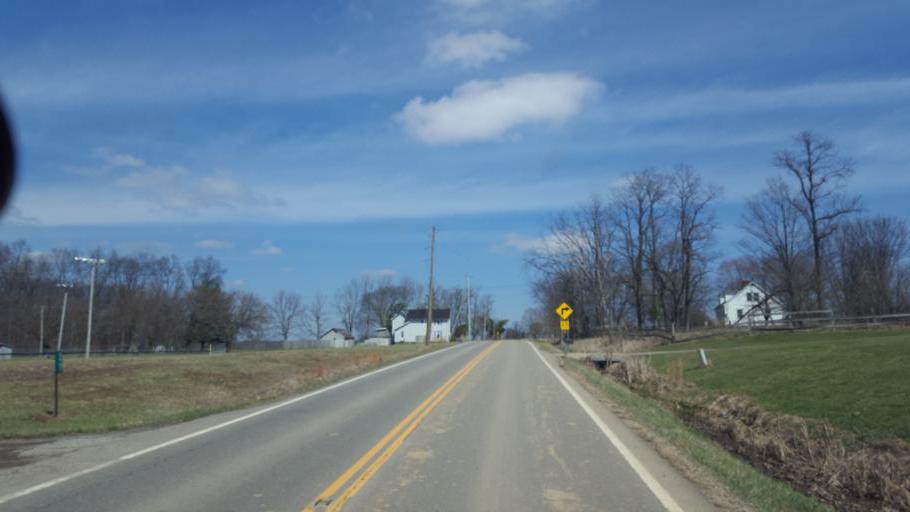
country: US
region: Ohio
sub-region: Richland County
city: Lincoln Heights
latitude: 40.8496
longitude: -82.4648
